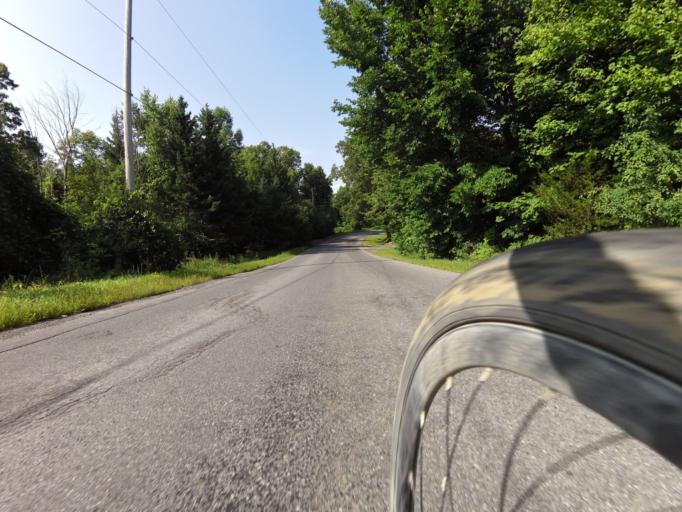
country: CA
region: Ontario
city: Kingston
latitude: 44.3343
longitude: -76.6667
